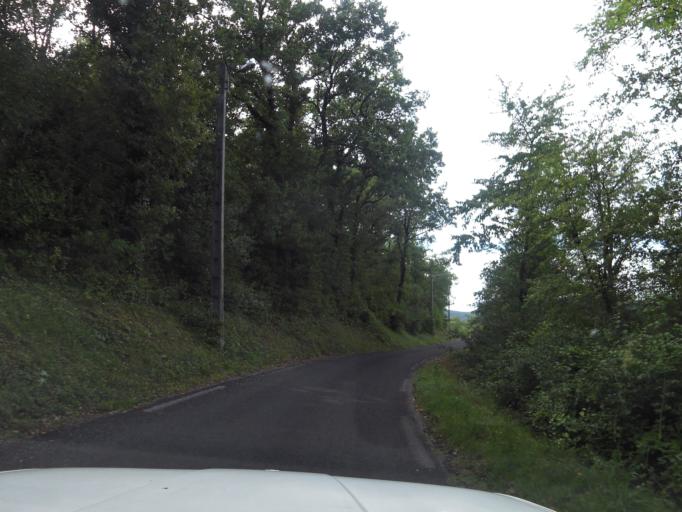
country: FR
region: Languedoc-Roussillon
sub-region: Departement du Gard
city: Saint-Christol-les-Ales
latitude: 44.0884
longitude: 4.0822
